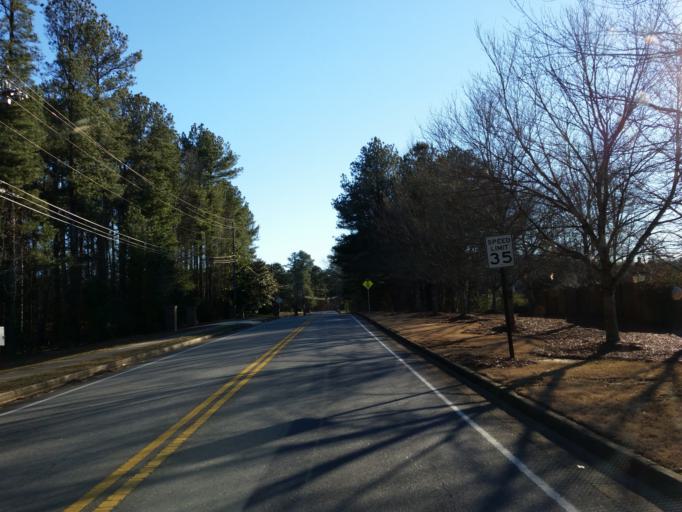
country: US
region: Georgia
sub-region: Cobb County
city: Kennesaw
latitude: 33.9761
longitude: -84.6906
